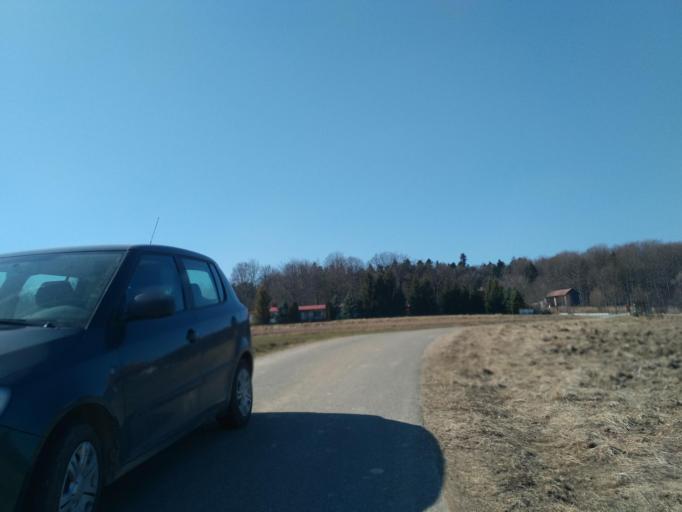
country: PL
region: Subcarpathian Voivodeship
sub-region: Powiat rzeszowski
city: Niechobrz
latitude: 49.9707
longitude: 21.8743
